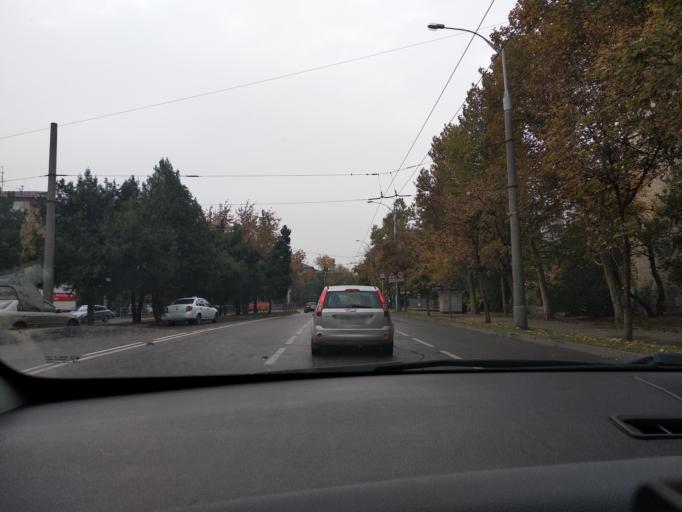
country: RU
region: Krasnodarskiy
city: Krasnodar
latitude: 45.0577
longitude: 38.9610
